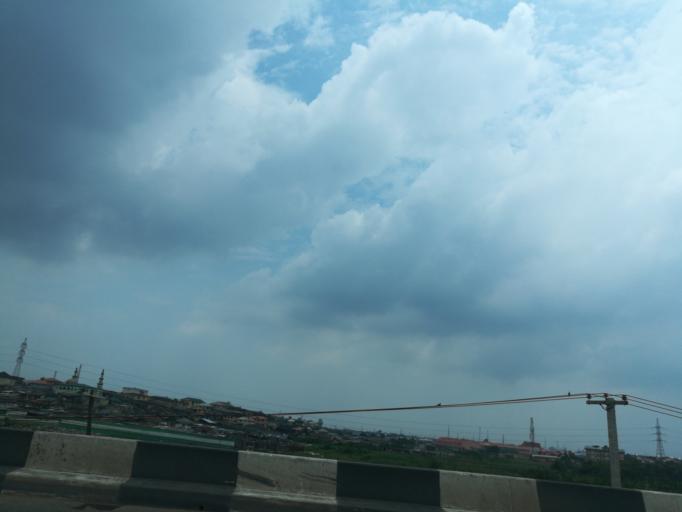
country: NG
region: Lagos
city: Ojota
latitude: 6.5803
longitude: 3.3735
